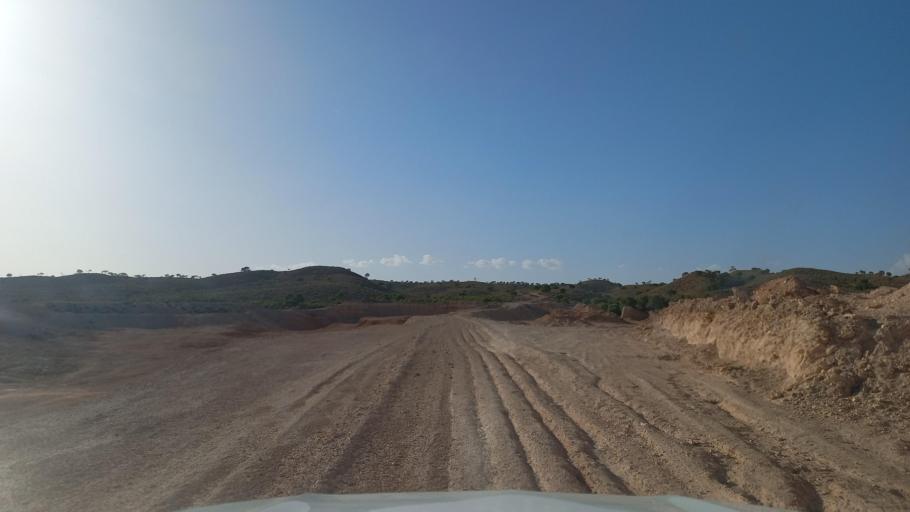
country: TN
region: Al Qasrayn
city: Sbiba
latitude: 35.3655
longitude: 8.9959
